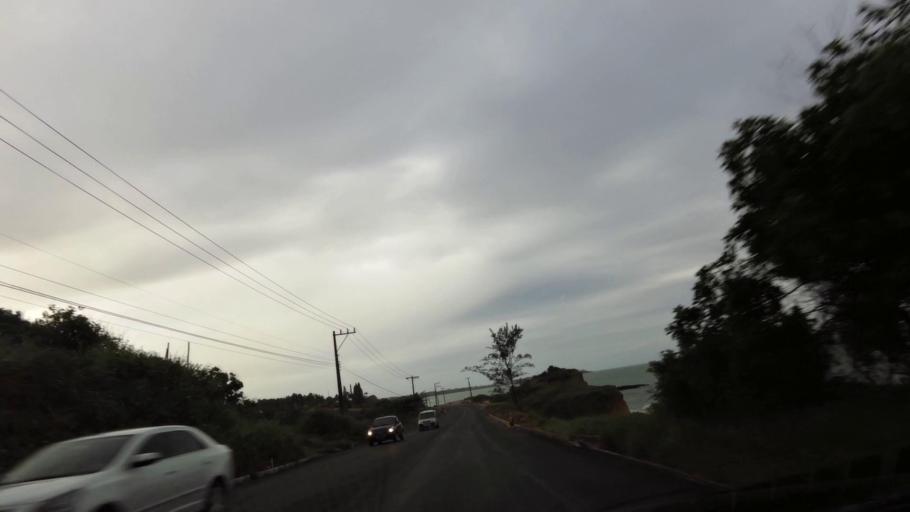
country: BR
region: Espirito Santo
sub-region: Guarapari
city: Guarapari
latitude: -20.7682
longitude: -40.5737
